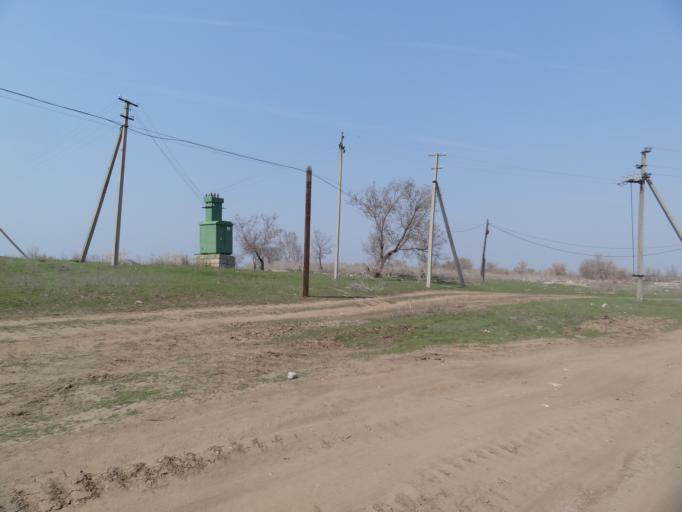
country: RU
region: Saratov
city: Privolzhskiy
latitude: 51.2855
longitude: 45.9489
